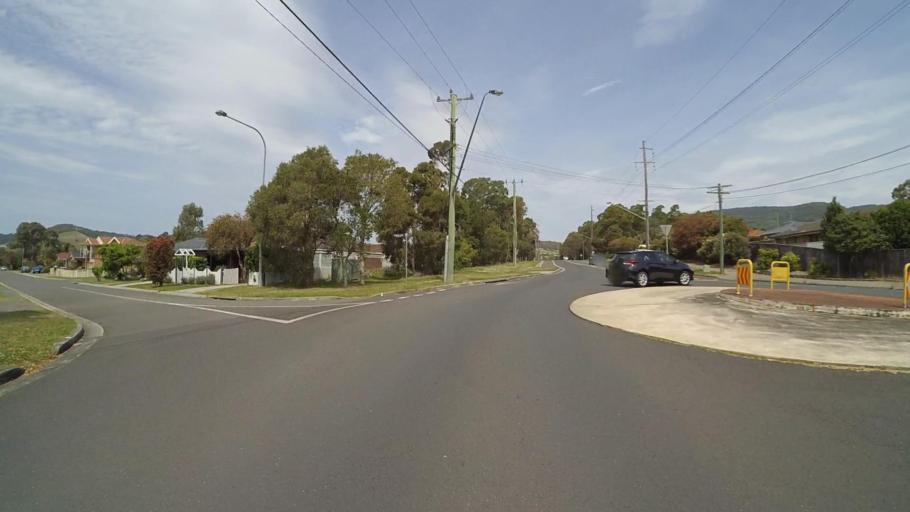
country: AU
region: New South Wales
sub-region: Shellharbour
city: Albion Park Rail
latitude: -34.5805
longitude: 150.7779
